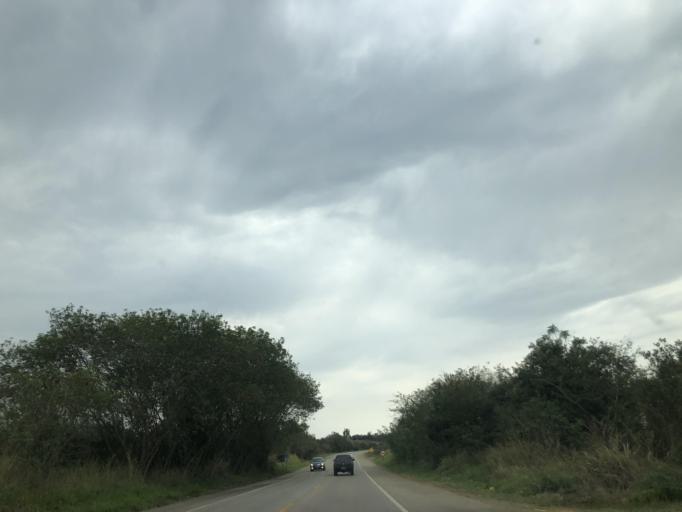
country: BR
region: Sao Paulo
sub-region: Salto De Pirapora
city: Salto de Pirapora
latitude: -23.7160
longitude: -47.6382
